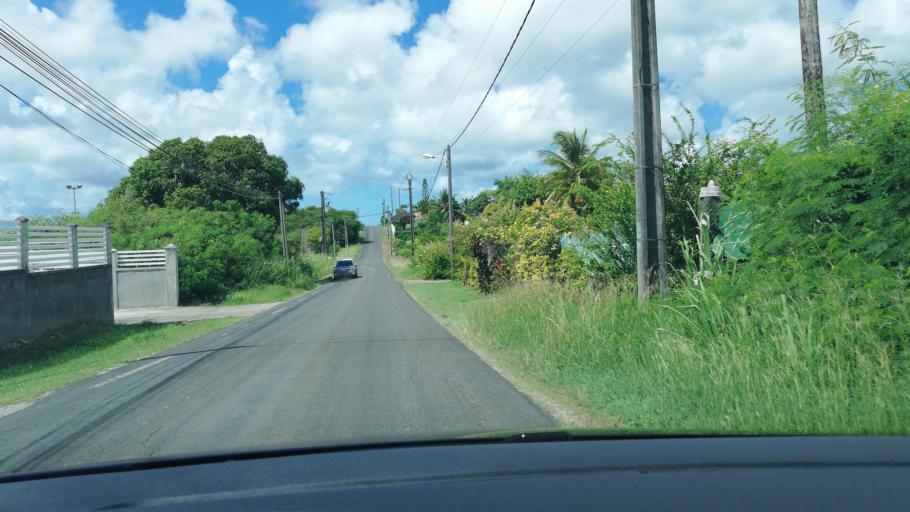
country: GP
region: Guadeloupe
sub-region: Guadeloupe
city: Petit-Canal
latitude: 16.3789
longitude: -61.4450
